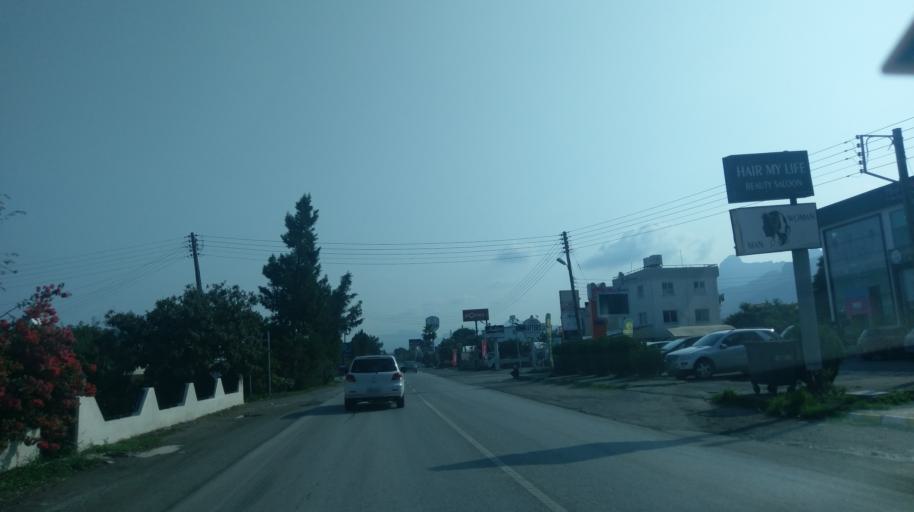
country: CY
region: Keryneia
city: Kyrenia
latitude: 35.3303
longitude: 33.3481
